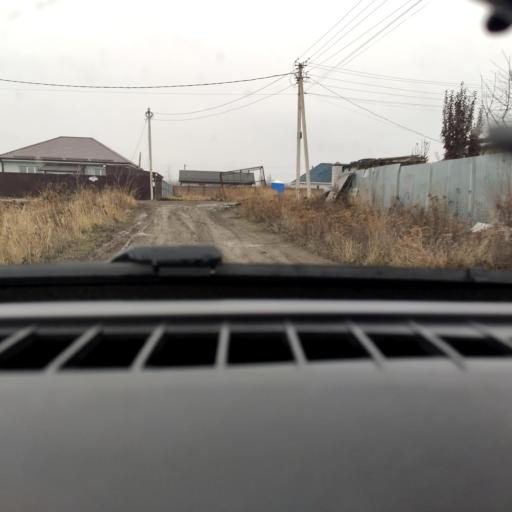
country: RU
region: Voronezj
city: Semiluki
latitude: 51.6612
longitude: 39.0440
